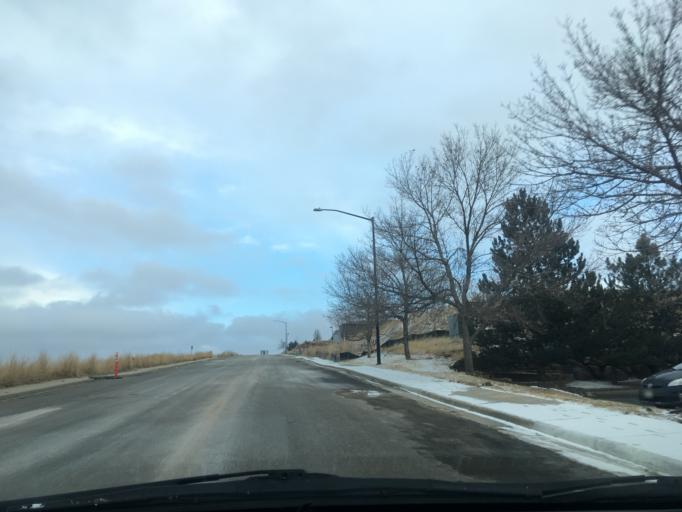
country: US
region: Colorado
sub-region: Boulder County
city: Lafayette
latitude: 39.9768
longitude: -105.0690
